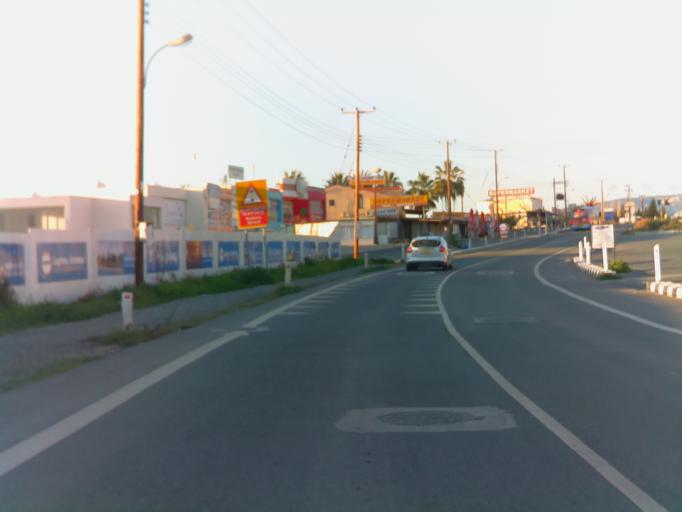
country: CY
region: Pafos
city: Kissonerga
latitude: 34.8228
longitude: 32.3927
